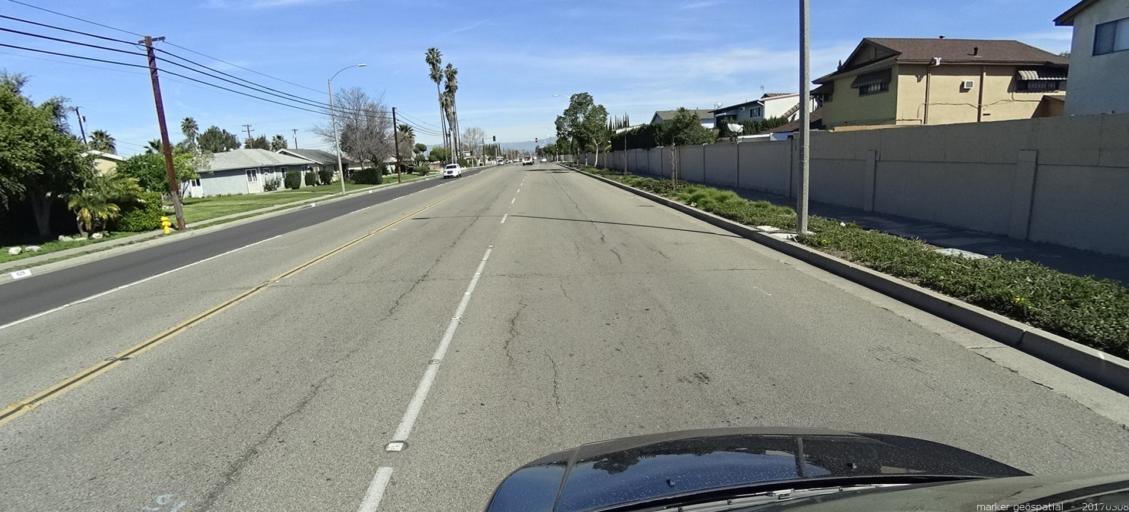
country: US
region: California
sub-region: Orange County
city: Stanton
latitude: 33.8235
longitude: -117.9846
